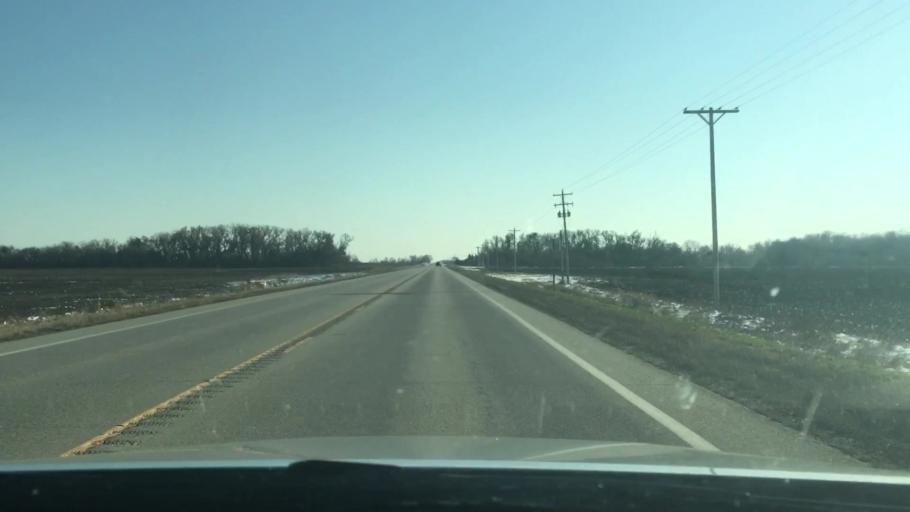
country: US
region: Kansas
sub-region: Rice County
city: Lyons
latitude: 38.3125
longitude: -98.2018
